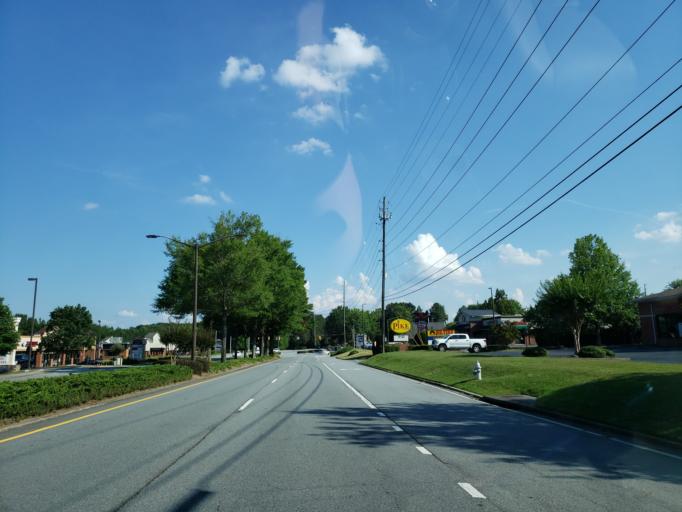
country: US
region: Georgia
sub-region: Cherokee County
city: Woodstock
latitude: 34.1150
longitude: -84.5541
